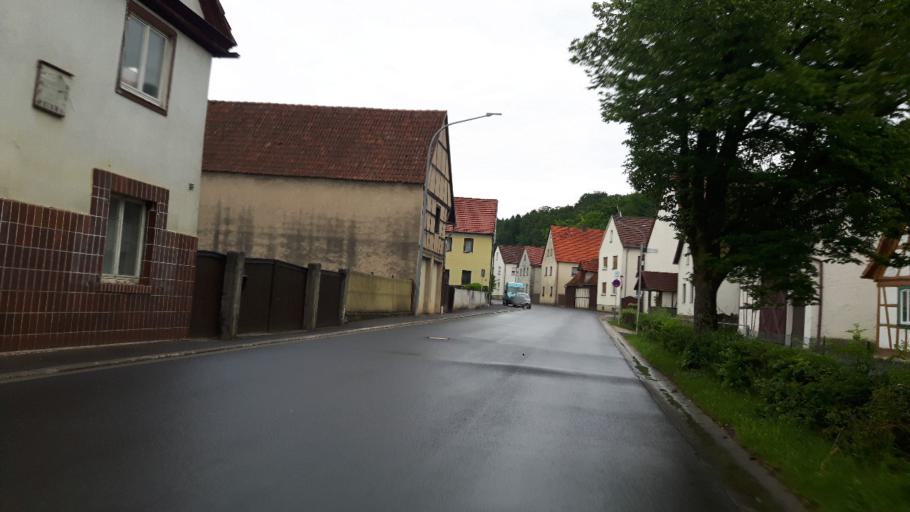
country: DE
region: Bavaria
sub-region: Regierungsbezirk Unterfranken
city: Uchtelhausen
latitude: 50.1142
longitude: 10.2688
